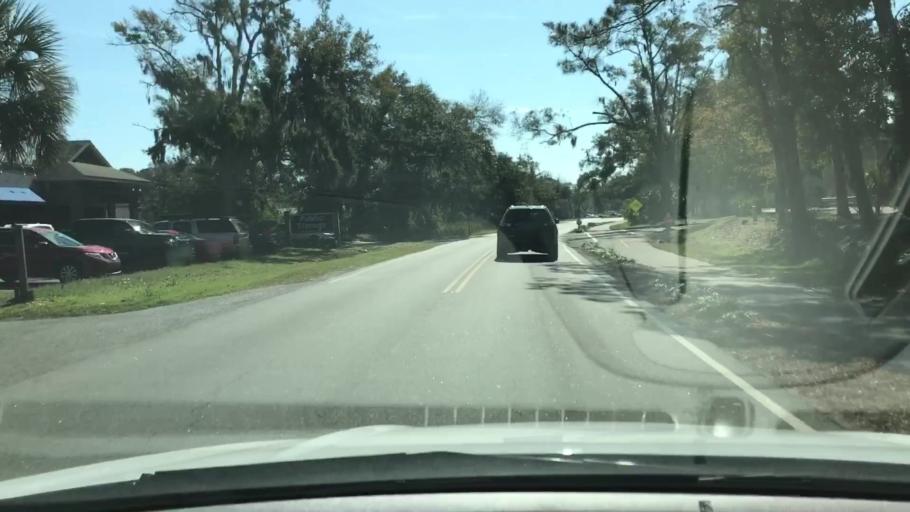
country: US
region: South Carolina
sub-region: Beaufort County
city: Hilton Head Island
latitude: 32.2180
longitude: -80.7032
